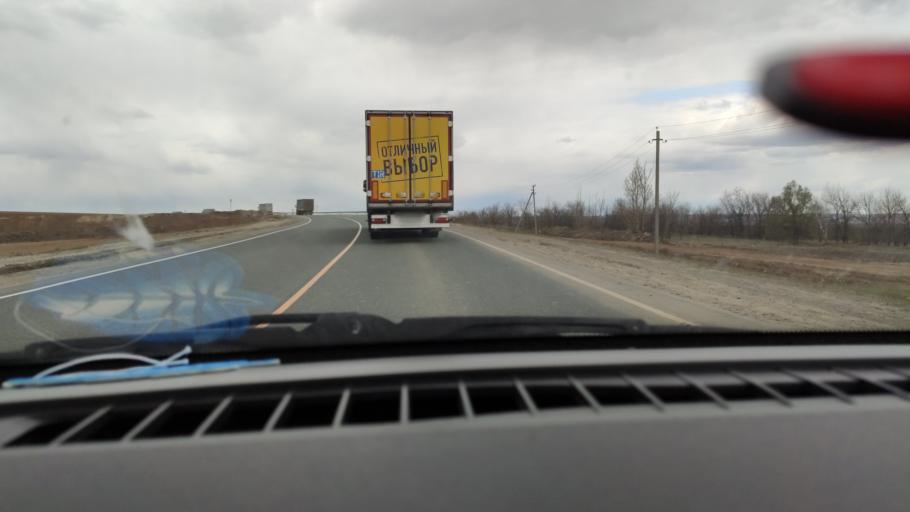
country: RU
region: Saratov
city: Sennoy
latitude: 52.1606
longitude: 47.0456
